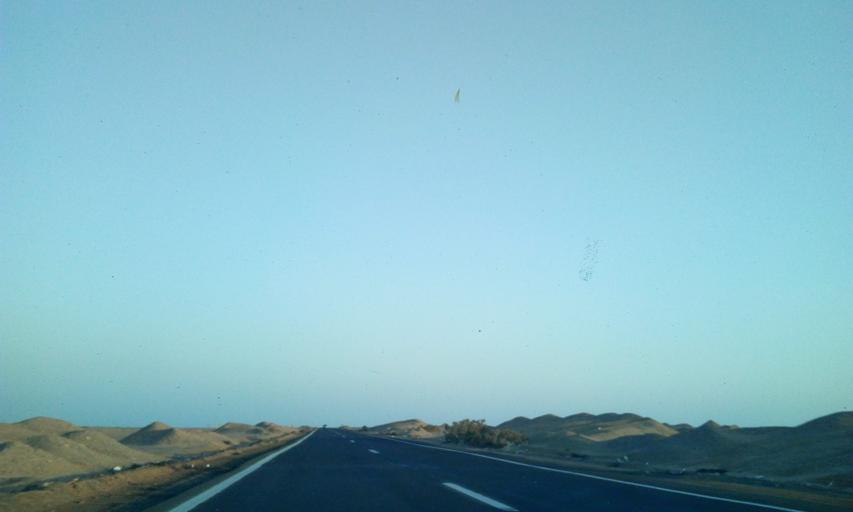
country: EG
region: South Sinai
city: Tor
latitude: 27.8057
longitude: 33.4652
